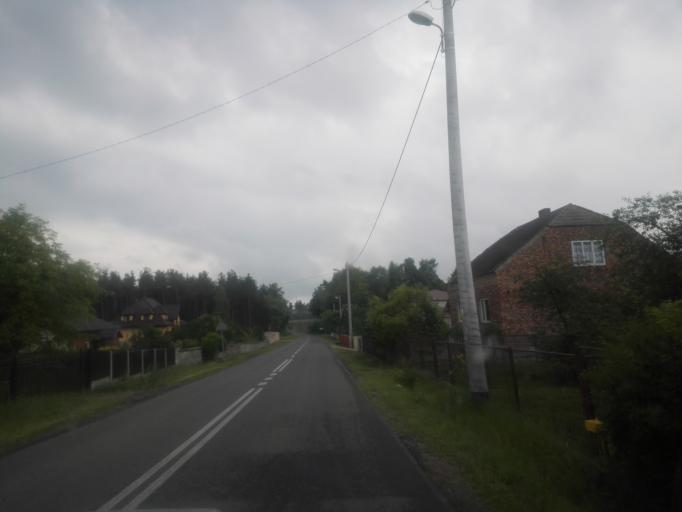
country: PL
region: Silesian Voivodeship
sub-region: Powiat czestochowski
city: Olsztyn
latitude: 50.7115
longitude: 19.3387
